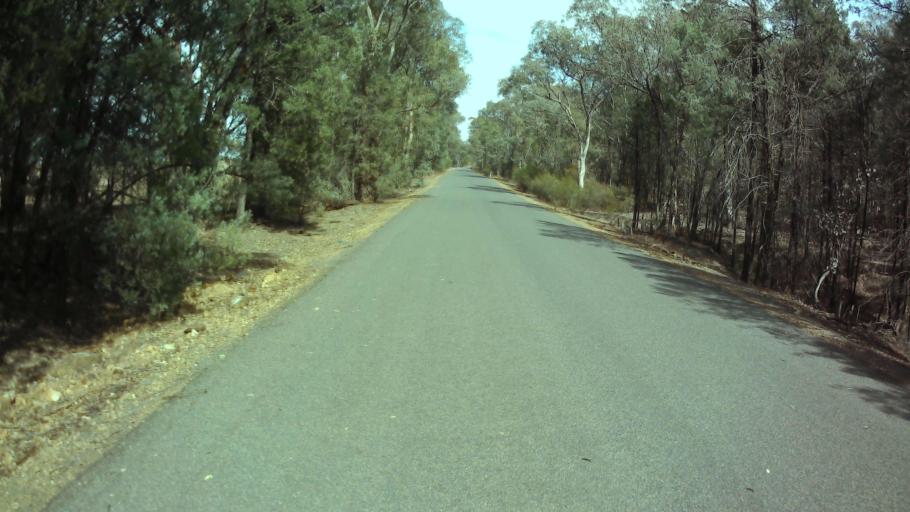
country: AU
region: New South Wales
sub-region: Weddin
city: Grenfell
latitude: -33.8053
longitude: 148.0374
